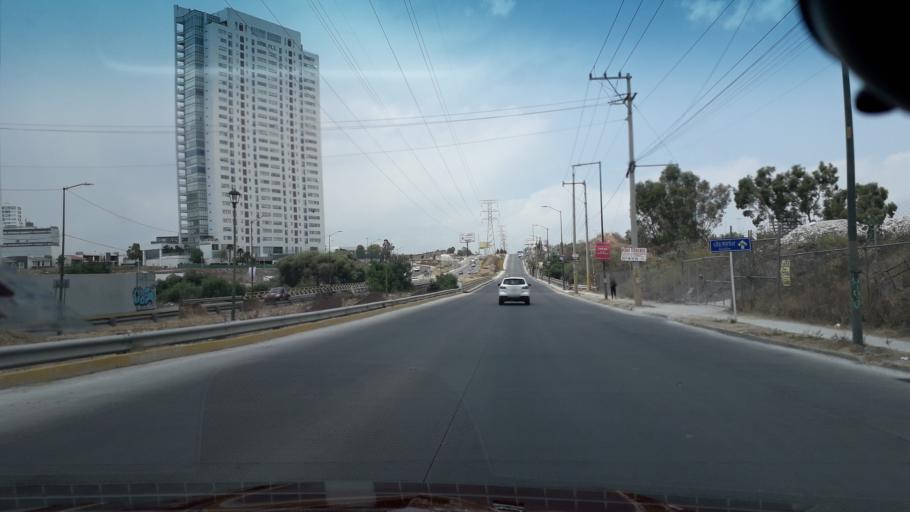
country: MX
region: Puebla
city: Tlazcalancingo
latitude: 19.0123
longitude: -98.2460
